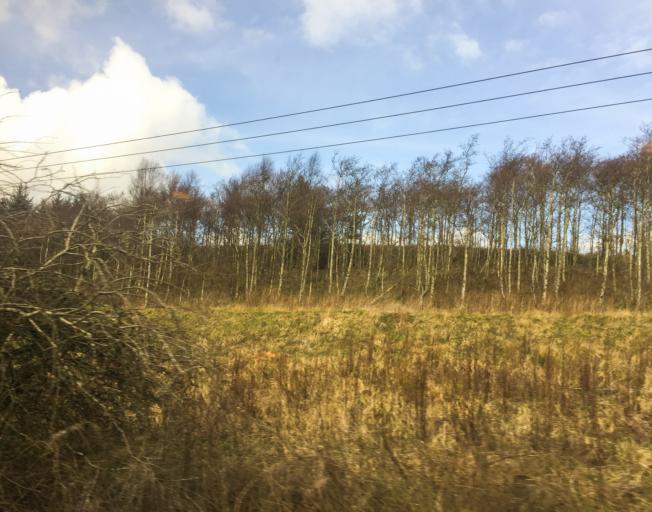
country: GB
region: Scotland
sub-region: North Lanarkshire
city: Glenboig
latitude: 55.8817
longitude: -4.0560
